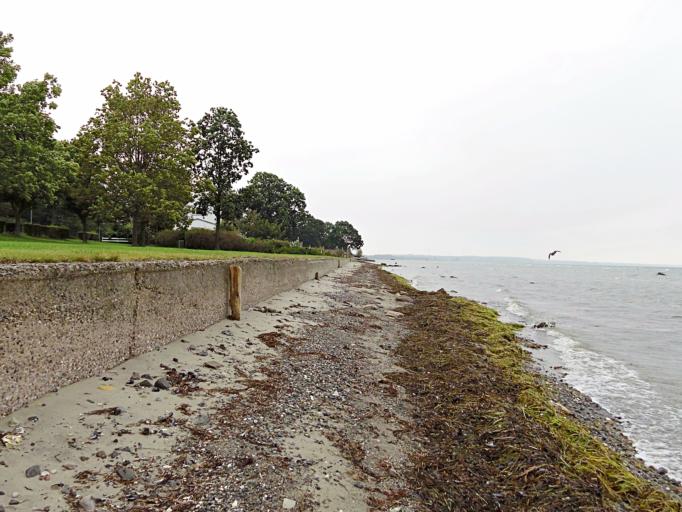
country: DK
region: Capital Region
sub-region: Fredensborg Kommune
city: Kokkedal
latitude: 55.9080
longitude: 12.5270
